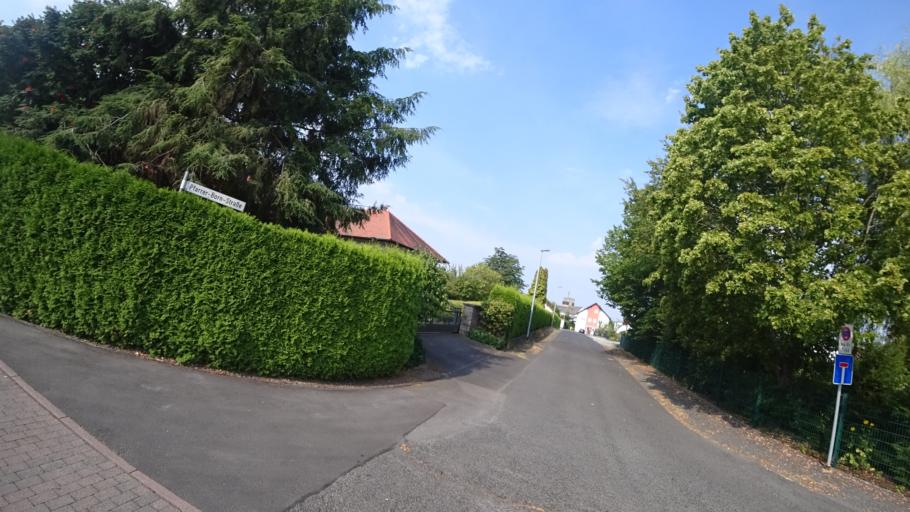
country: DE
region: Rheinland-Pfalz
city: Ransbach-Baumbach
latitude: 50.4564
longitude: 7.7258
